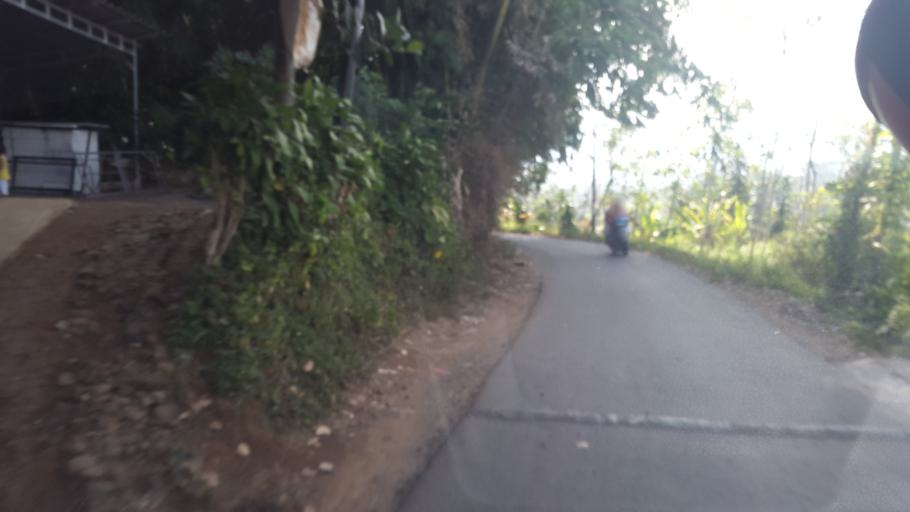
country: ID
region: West Java
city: Cicurug
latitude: -6.8312
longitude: 106.7326
